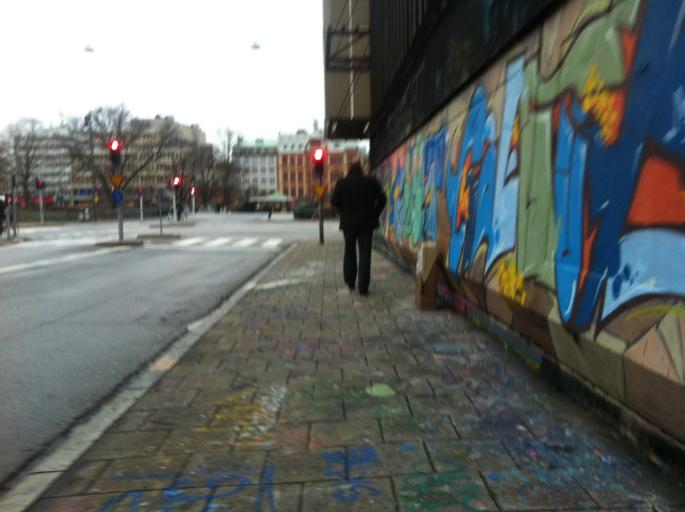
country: SE
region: Skane
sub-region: Malmo
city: Malmoe
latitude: 55.6000
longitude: 13.0050
